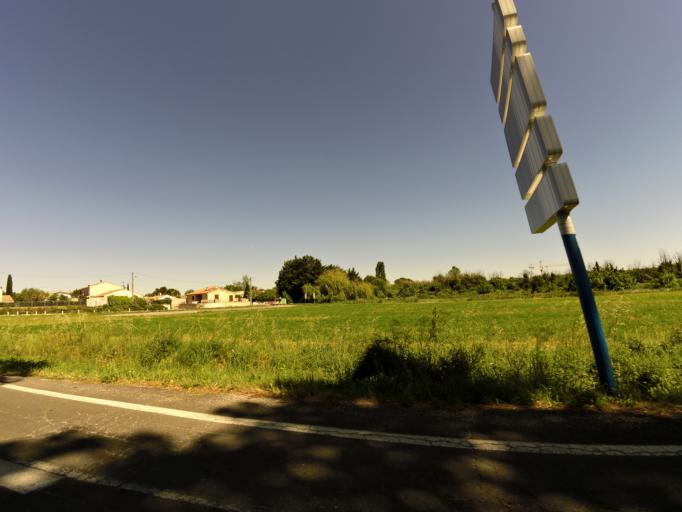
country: FR
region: Languedoc-Roussillon
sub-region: Departement de l'Herault
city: Castries
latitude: 43.6729
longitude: 3.9816
